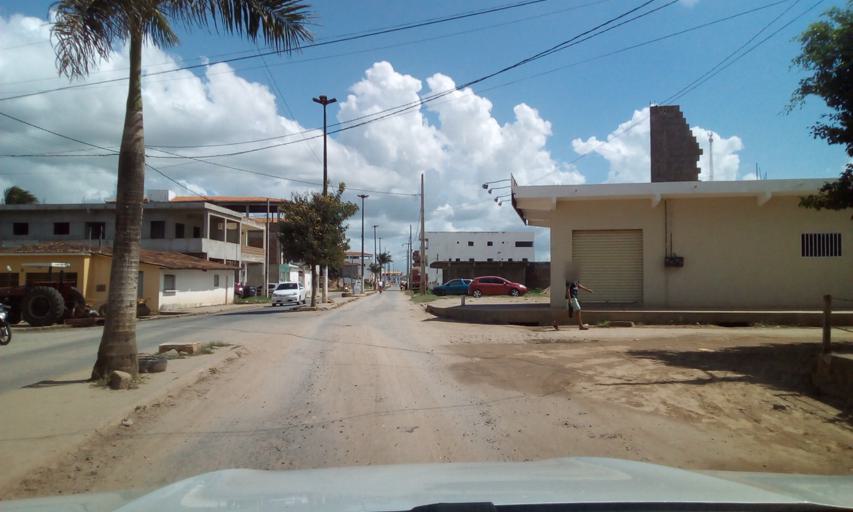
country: BR
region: Paraiba
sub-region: Guarabira
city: Guarabira
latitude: -6.8506
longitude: -35.3777
